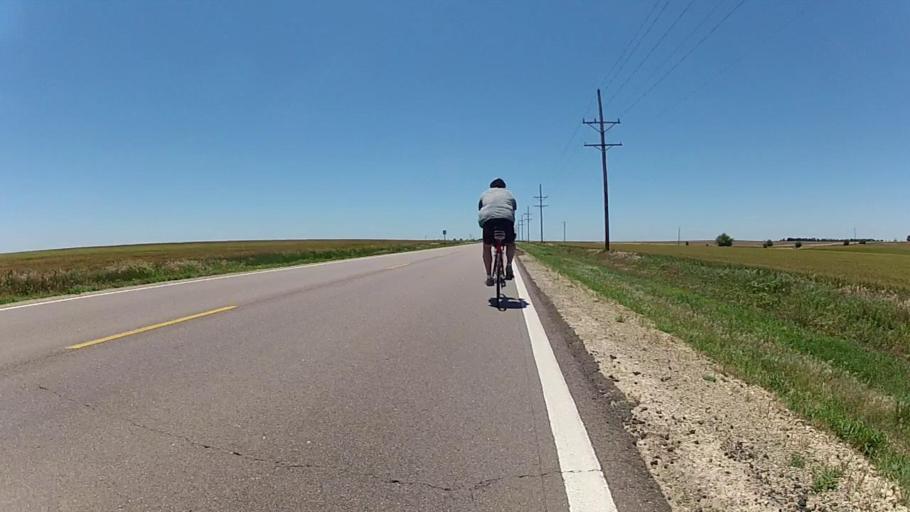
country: US
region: Kansas
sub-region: Kiowa County
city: Greensburg
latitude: 37.5294
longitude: -99.3208
